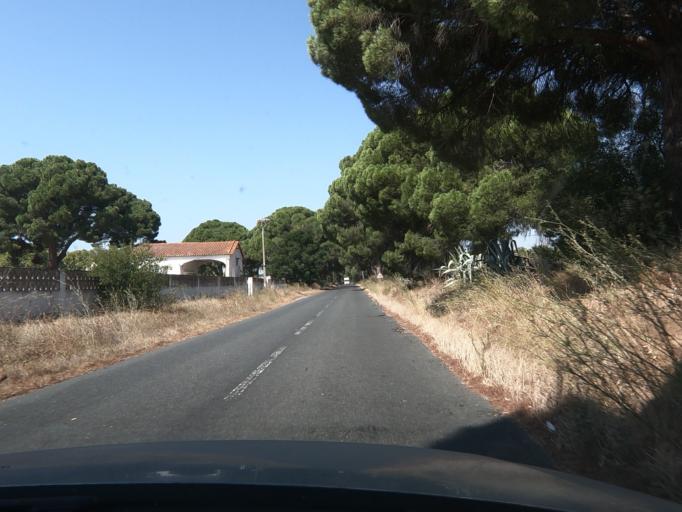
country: PT
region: Setubal
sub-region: Alcacer do Sal
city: Alcacer do Sal
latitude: 38.2797
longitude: -8.3959
